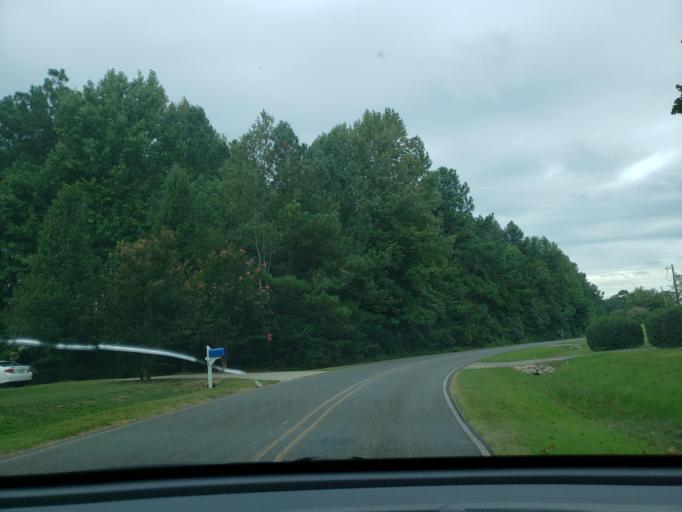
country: US
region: North Carolina
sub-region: Vance County
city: Henderson
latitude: 36.4015
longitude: -78.3745
